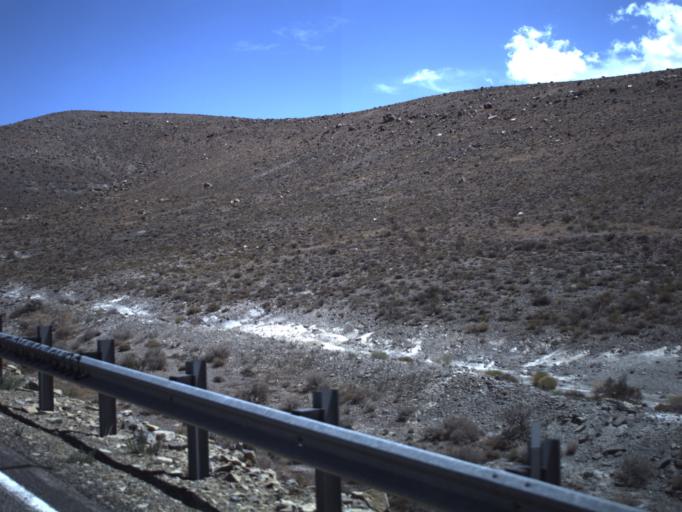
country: US
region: Utah
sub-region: Beaver County
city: Milford
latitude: 39.0267
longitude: -113.3478
